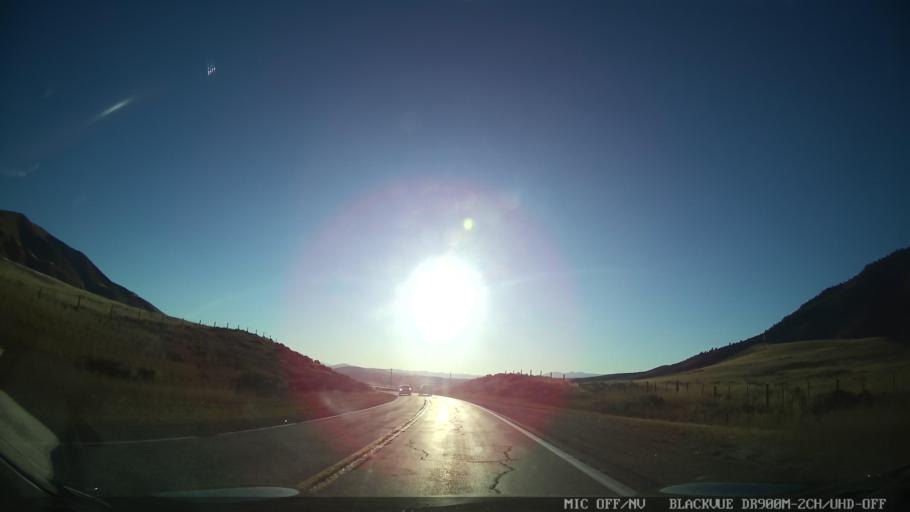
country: US
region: Colorado
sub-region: Grand County
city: Kremmling
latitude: 40.0508
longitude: -106.3529
